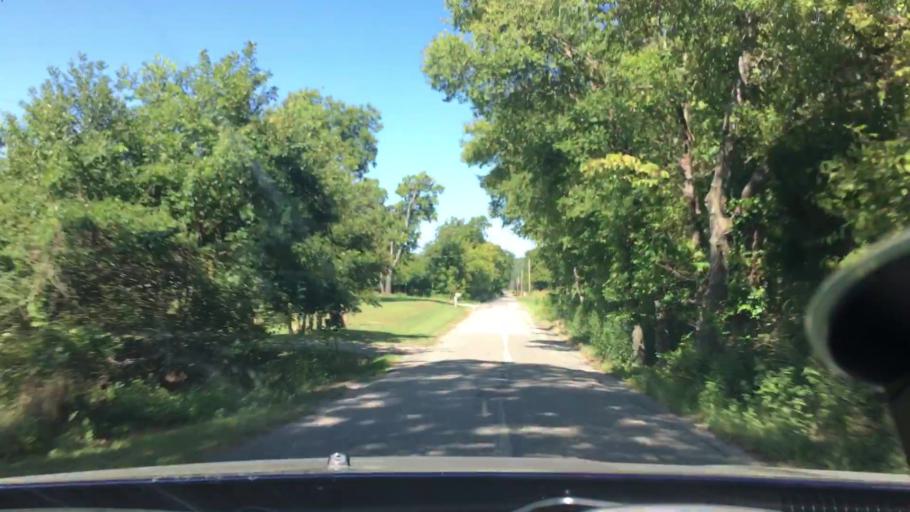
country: US
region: Oklahoma
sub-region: Pontotoc County
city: Ada
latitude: 34.7236
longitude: -96.6601
